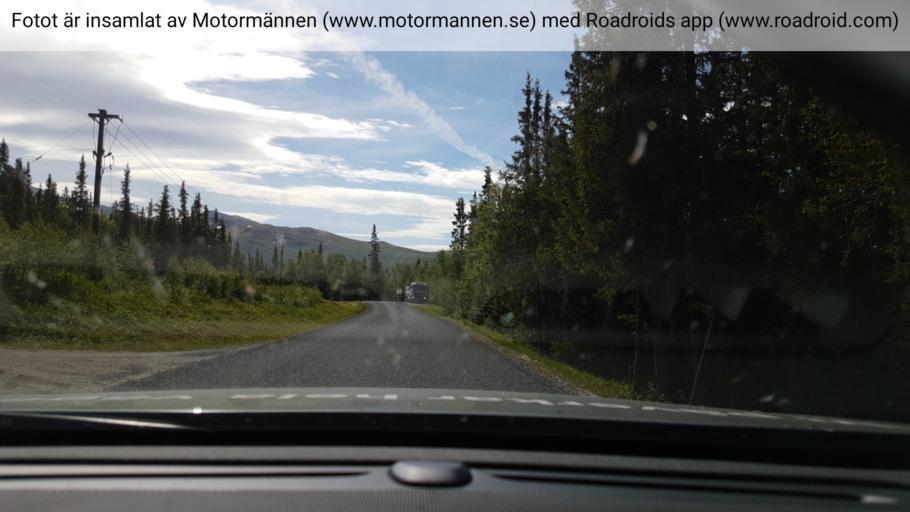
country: SE
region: Vaesterbotten
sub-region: Vilhelmina Kommun
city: Sjoberg
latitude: 65.2716
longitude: 15.3683
